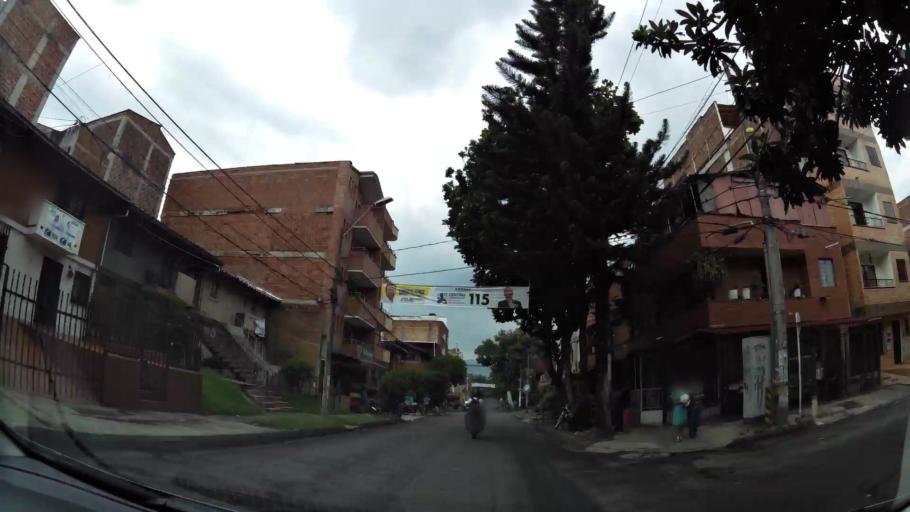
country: CO
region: Antioquia
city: Itagui
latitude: 6.1839
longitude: -75.5956
